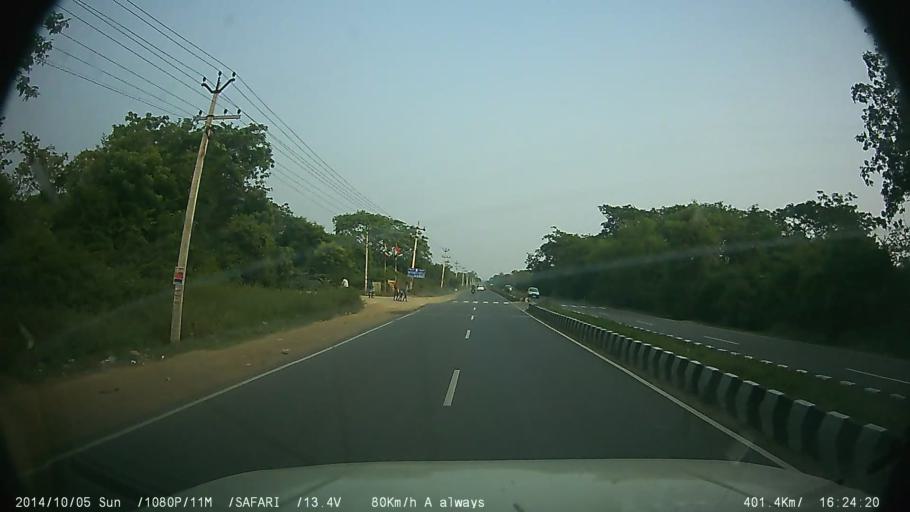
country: IN
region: Tamil Nadu
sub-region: Kancheepuram
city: Vengavasal
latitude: 12.8238
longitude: 80.1694
